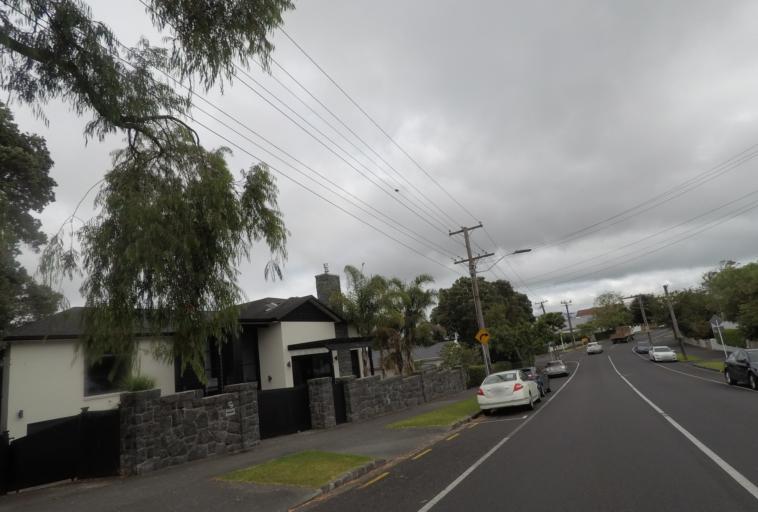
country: NZ
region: Auckland
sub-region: Auckland
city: Auckland
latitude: -36.8790
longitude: 174.7573
